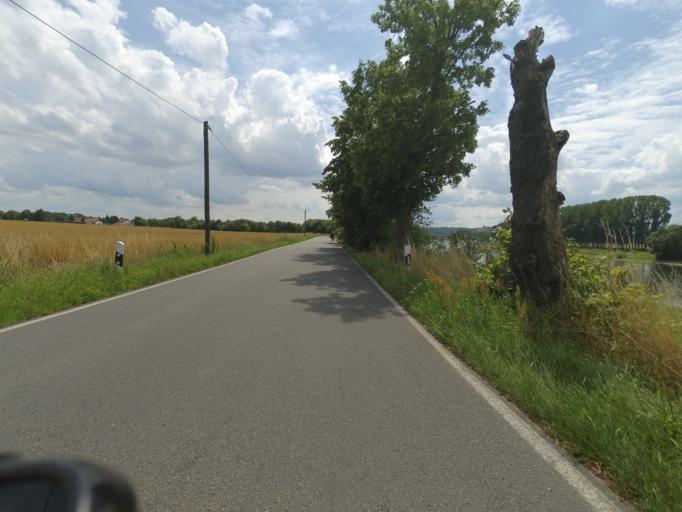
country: DE
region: Saxony
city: Heidenau
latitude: 50.9856
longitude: 13.8853
